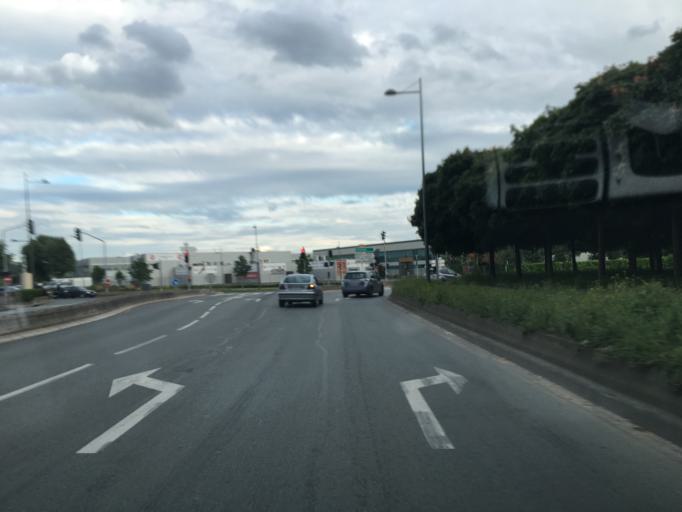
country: FR
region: Ile-de-France
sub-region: Departement du Val-de-Marne
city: Bonneuil-sur-Marne
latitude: 48.7734
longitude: 2.4901
